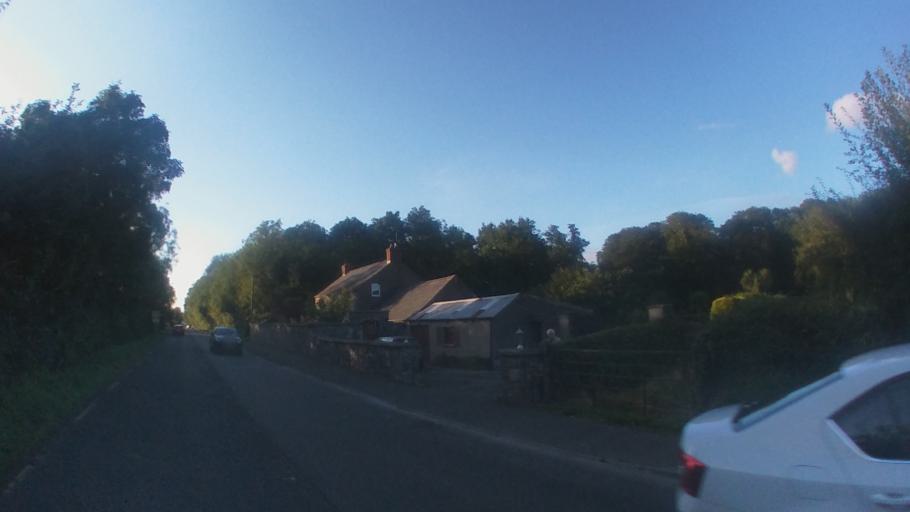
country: IE
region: Leinster
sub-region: Lu
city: Blackrock
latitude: 54.0184
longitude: -6.3286
